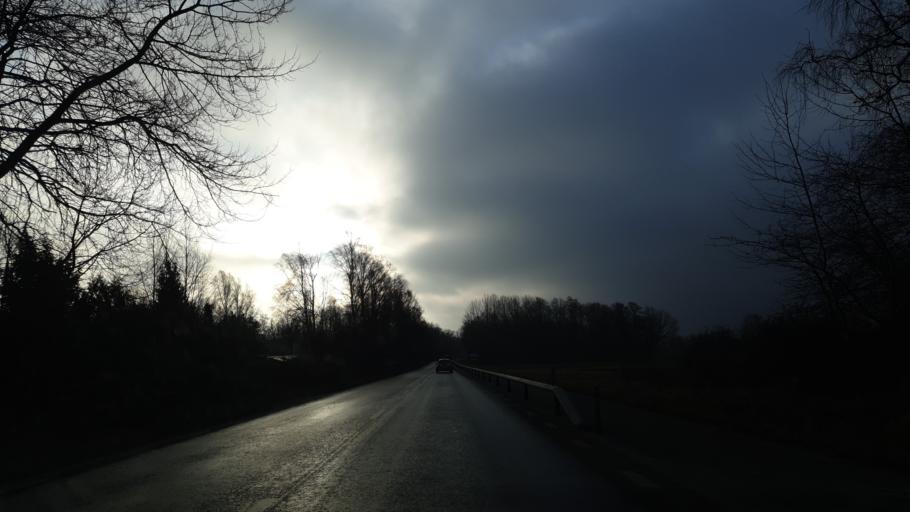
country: SE
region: Blekinge
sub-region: Karlshamns Kommun
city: Morrum
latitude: 56.1349
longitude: 14.6720
